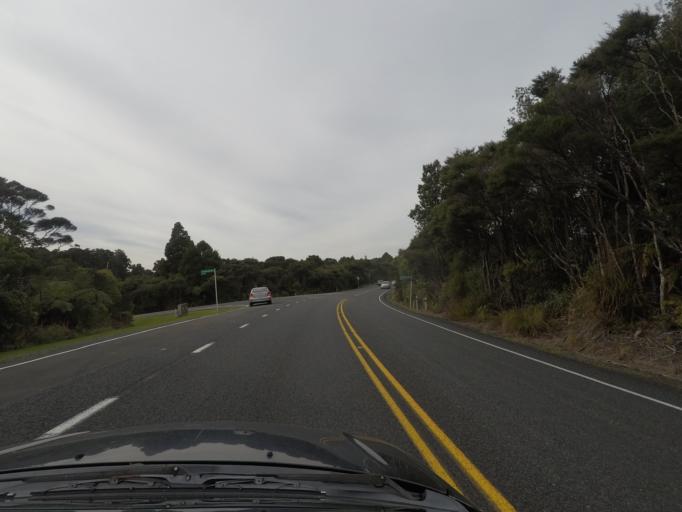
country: NZ
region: Auckland
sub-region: Auckland
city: Titirangi
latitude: -36.9457
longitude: 174.5262
